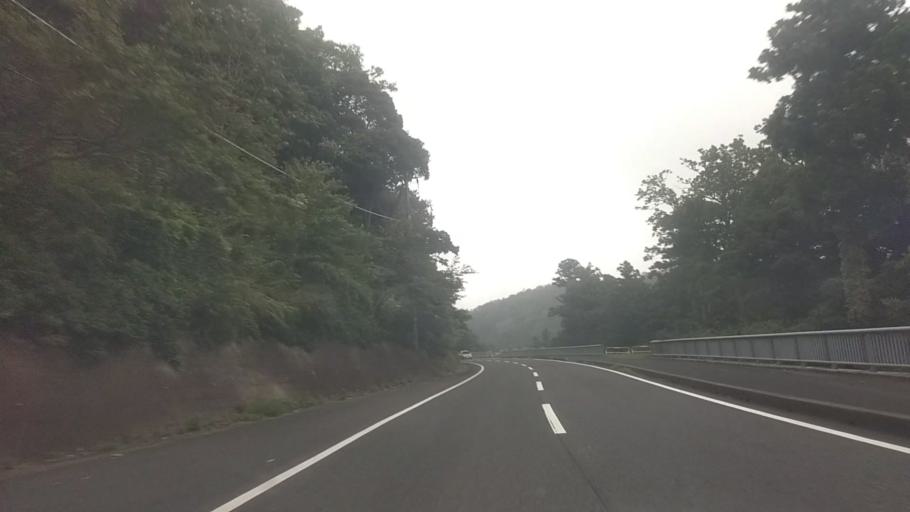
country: JP
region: Chiba
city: Kawaguchi
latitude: 35.1439
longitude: 140.1507
